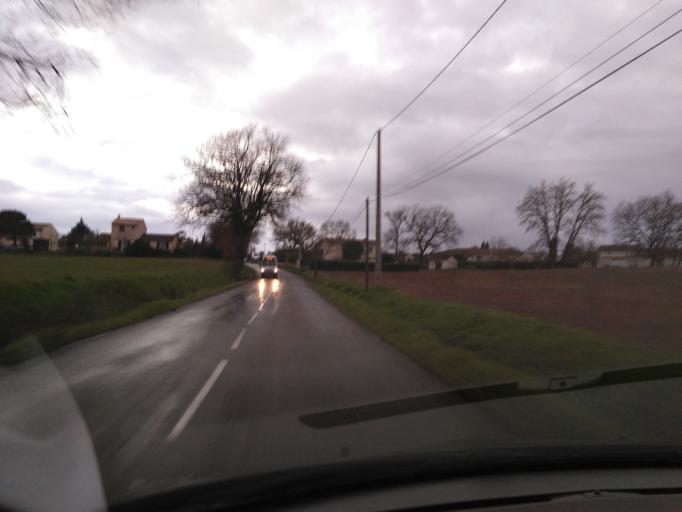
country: FR
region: Midi-Pyrenees
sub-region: Departement de la Haute-Garonne
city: Aussonne
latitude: 43.6844
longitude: 1.3341
